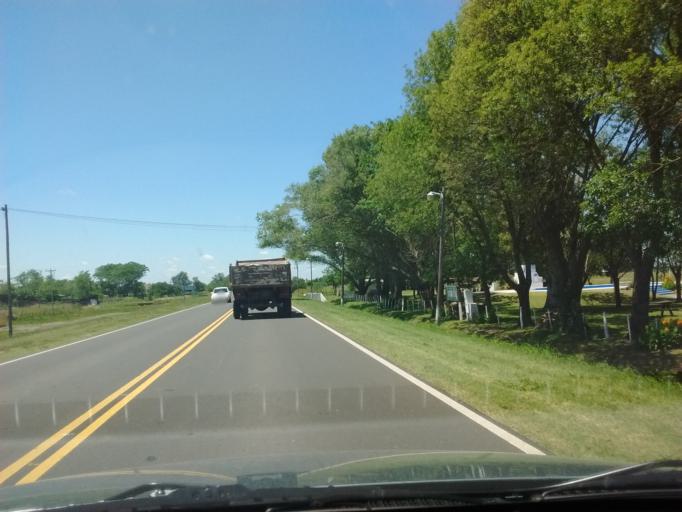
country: AR
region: Entre Rios
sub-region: Departamento de Gualeguay
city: Gualeguay
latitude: -33.0993
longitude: -59.3729
